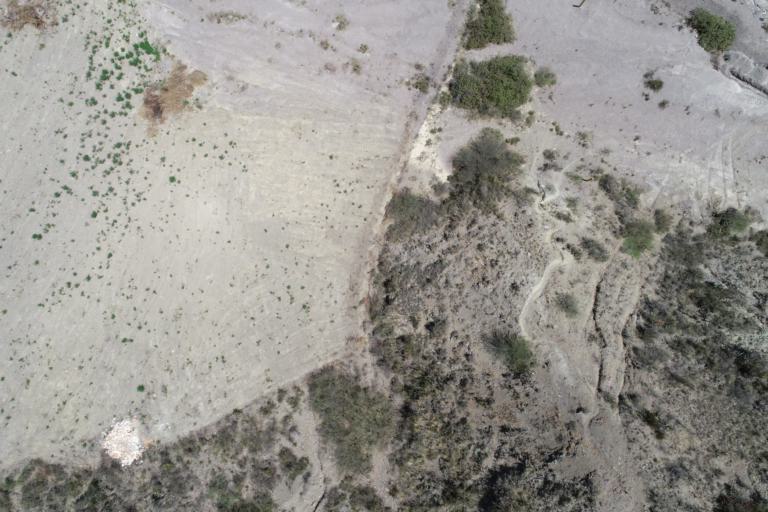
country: BO
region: La Paz
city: La Paz
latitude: -16.6421
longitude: -68.0402
